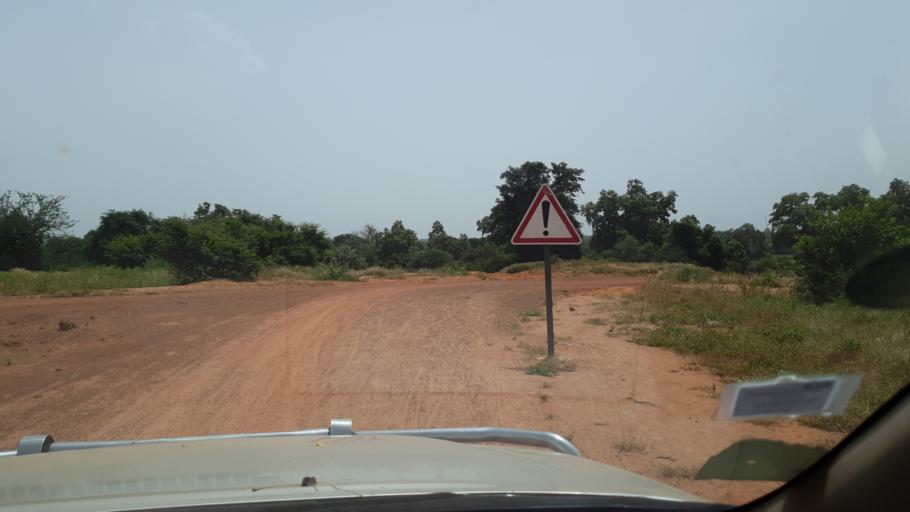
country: ML
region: Koulikoro
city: Kolokani
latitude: 13.4254
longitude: -8.2407
